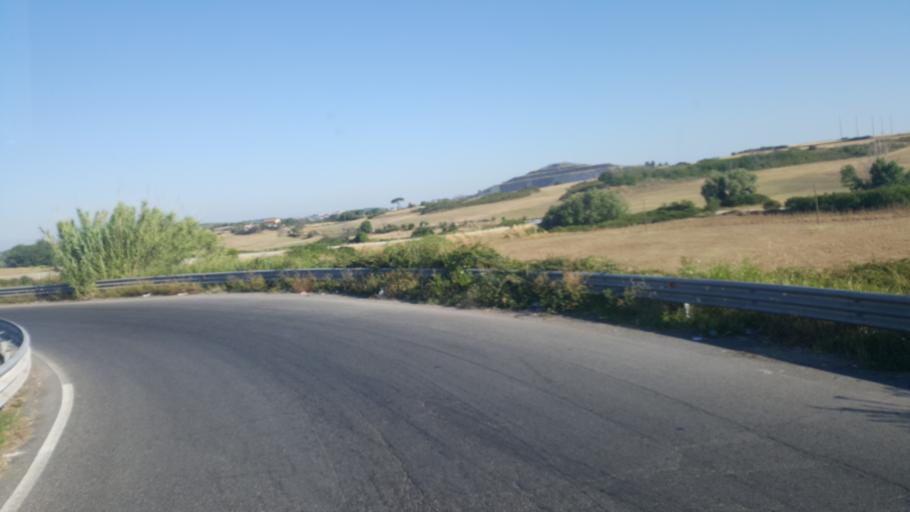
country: IT
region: Latium
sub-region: Citta metropolitana di Roma Capitale
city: Albuccione
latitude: 41.9706
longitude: 12.6900
